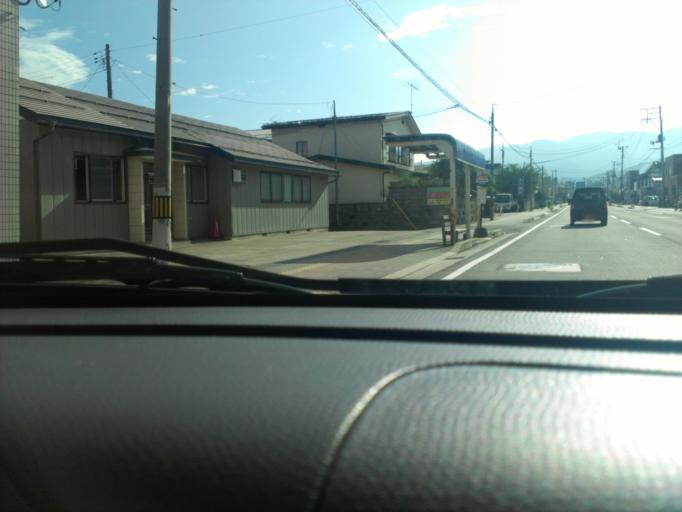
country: JP
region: Fukushima
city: Kitakata
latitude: 37.4856
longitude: 139.9229
